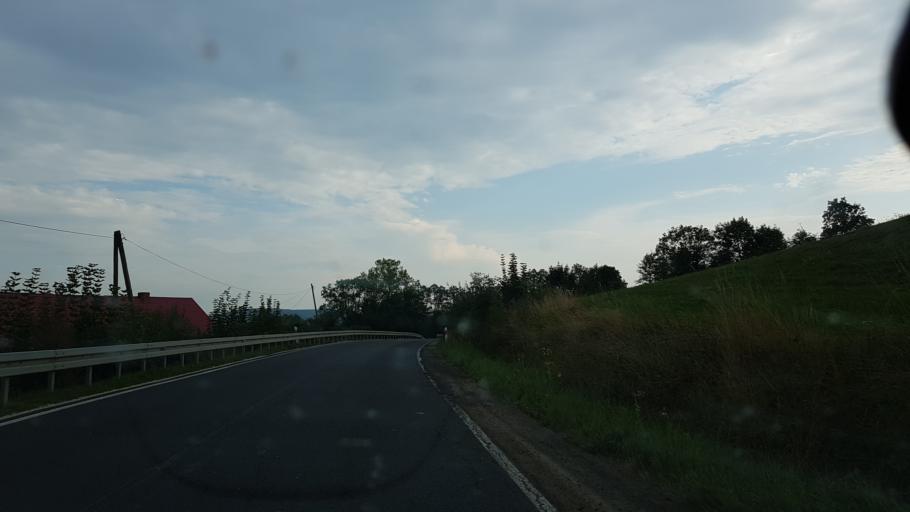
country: PL
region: Lower Silesian Voivodeship
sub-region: Powiat kamiennogorski
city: Marciszow
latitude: 50.8849
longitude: 15.9962
